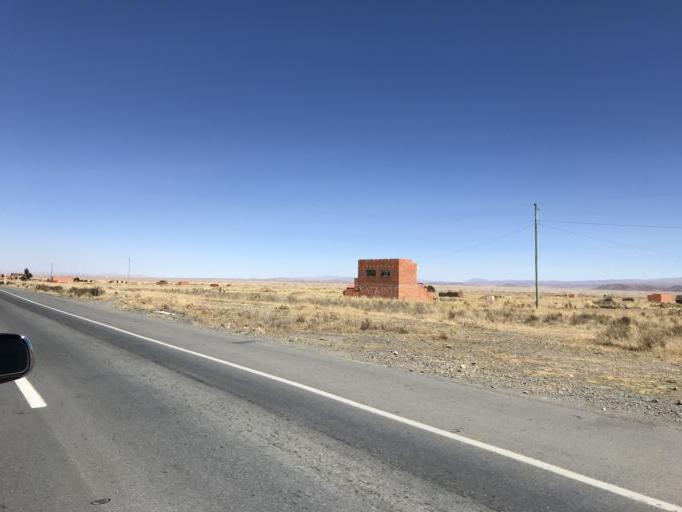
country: BO
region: La Paz
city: Batallas
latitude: -16.3707
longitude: -68.3856
